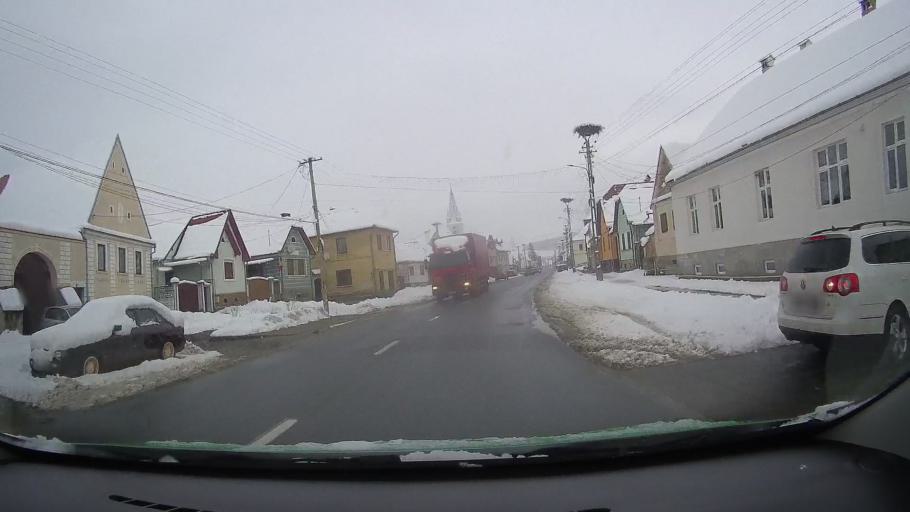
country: RO
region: Sibiu
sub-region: Comuna Cristian
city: Cristian
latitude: 45.7817
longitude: 24.0278
